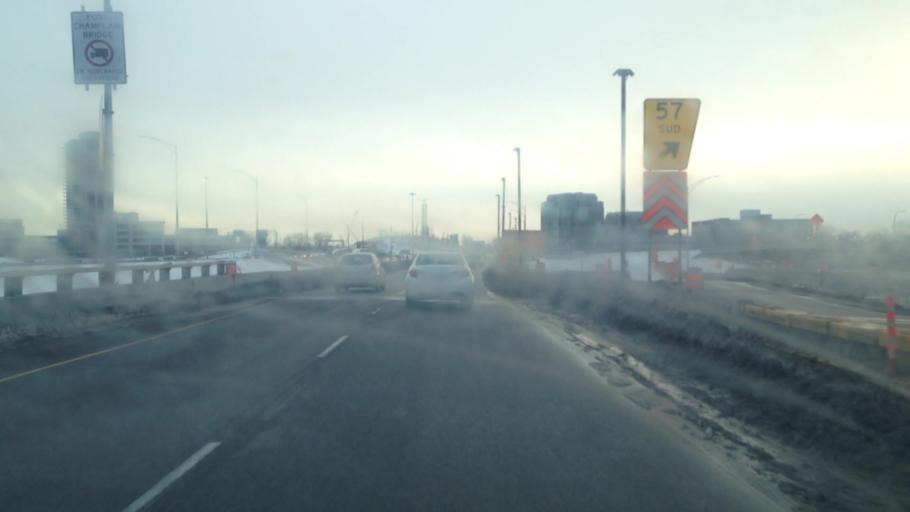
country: CA
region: Quebec
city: Westmount
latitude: 45.4706
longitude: -73.5475
